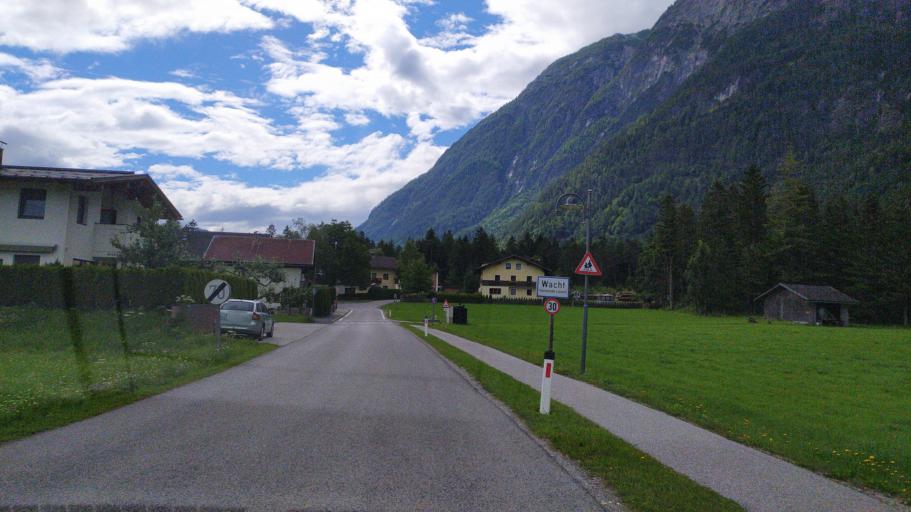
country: AT
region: Tyrol
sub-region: Politischer Bezirk Lienz
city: Lavant
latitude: 46.7918
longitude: 12.8588
